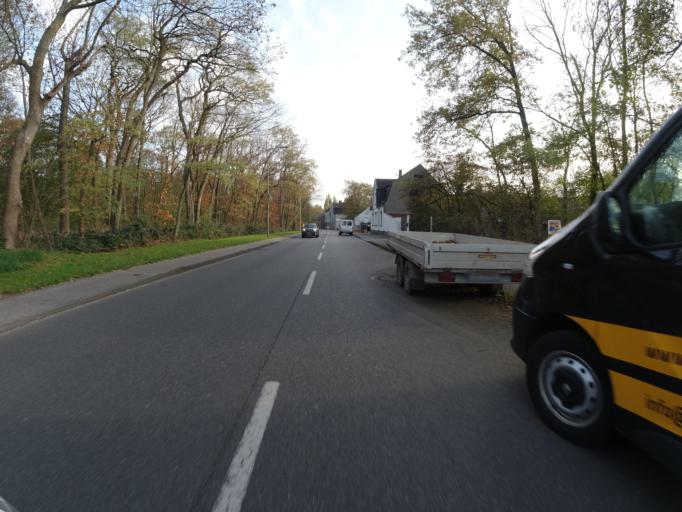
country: DE
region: North Rhine-Westphalia
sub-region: Regierungsbezirk Dusseldorf
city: Hochfeld
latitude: 51.4032
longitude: 6.6918
